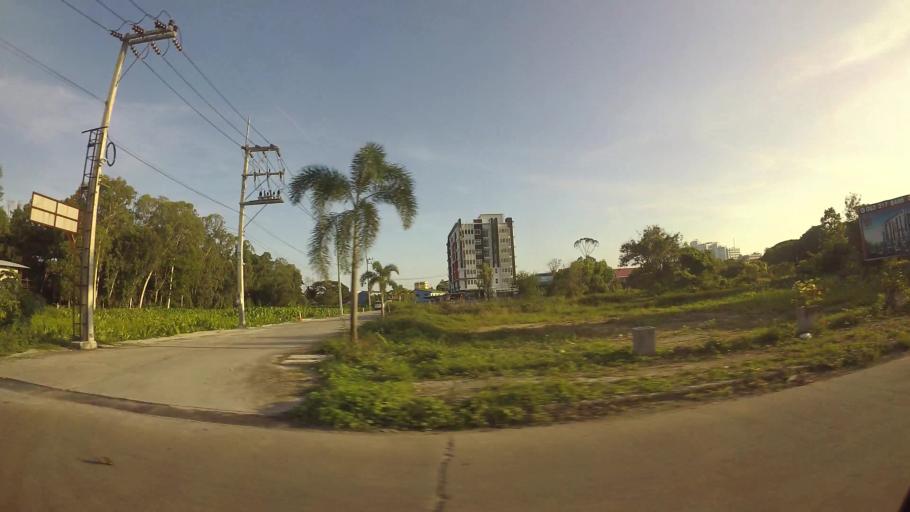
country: TH
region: Rayong
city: Rayong
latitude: 12.6863
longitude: 101.2820
